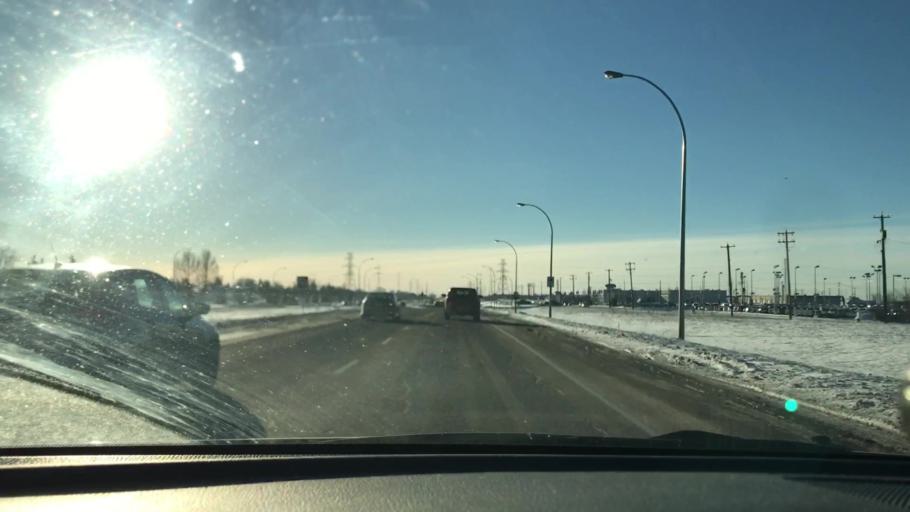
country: CA
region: Alberta
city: Edmonton
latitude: 53.4679
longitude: -113.4669
